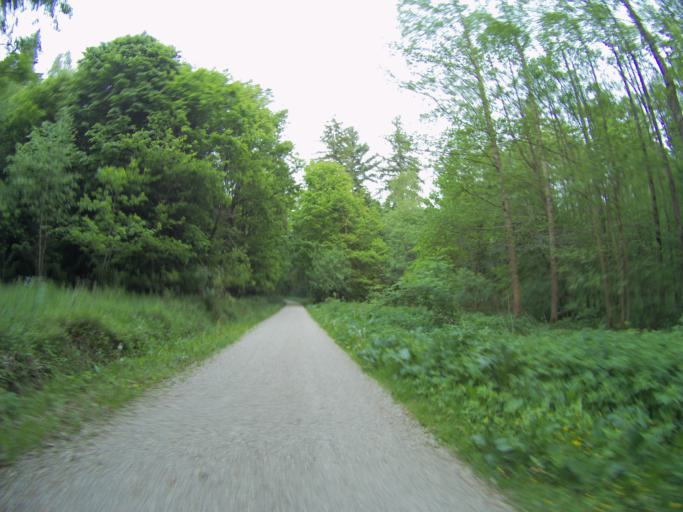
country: DE
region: Bavaria
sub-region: Upper Bavaria
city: Freising
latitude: 48.4196
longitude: 11.7433
